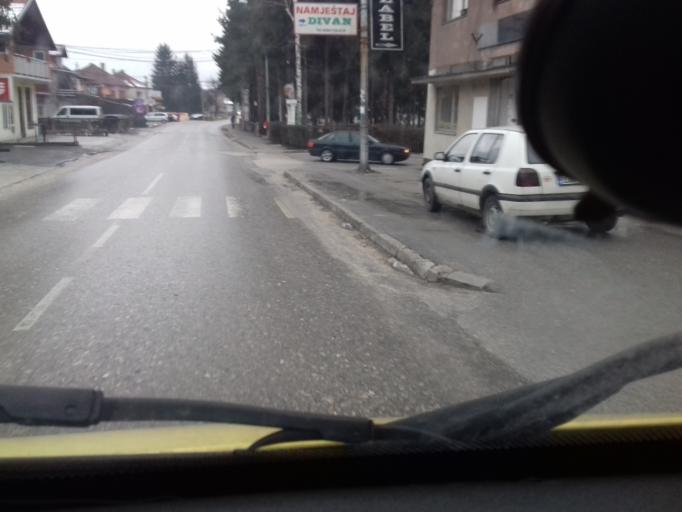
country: BA
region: Federation of Bosnia and Herzegovina
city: Vitez
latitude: 44.1576
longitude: 17.7878
